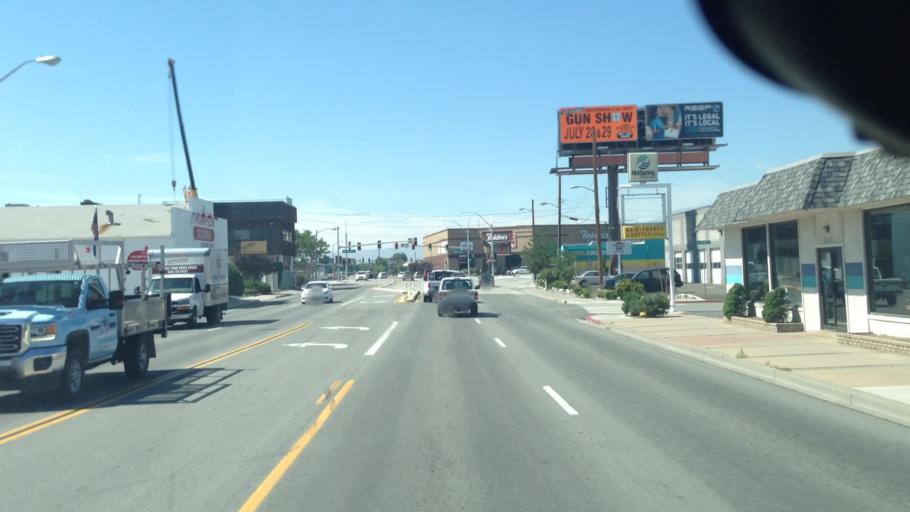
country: US
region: Nevada
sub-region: Washoe County
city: Sparks
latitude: 39.5292
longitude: -119.7665
